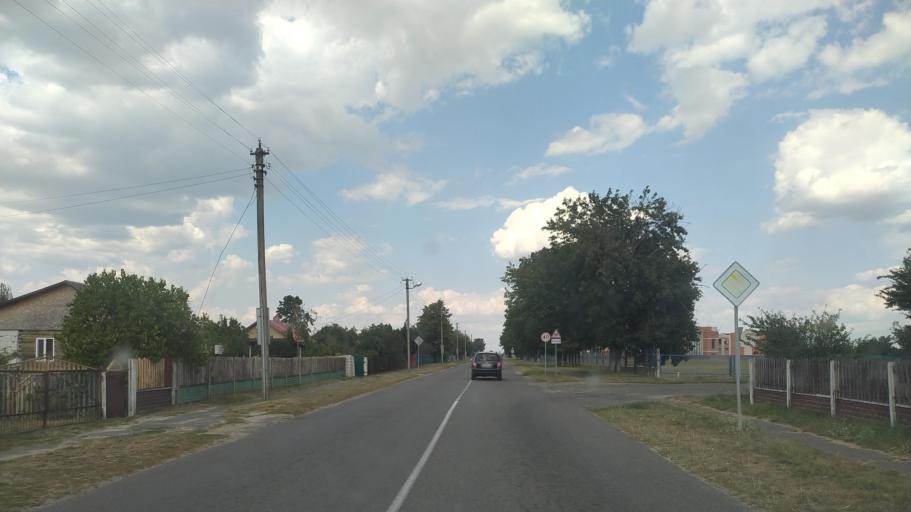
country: BY
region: Brest
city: Drahichyn
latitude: 52.1131
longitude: 25.1153
